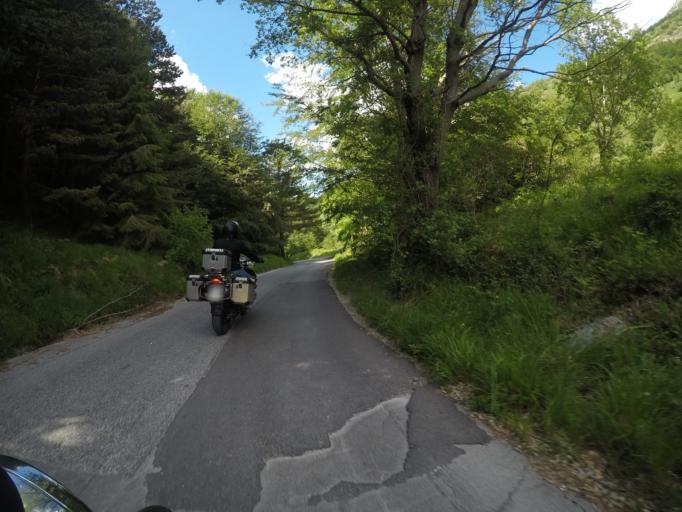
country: IT
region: Tuscany
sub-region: Provincia di Lucca
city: Minucciano
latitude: 44.1388
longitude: 10.1959
